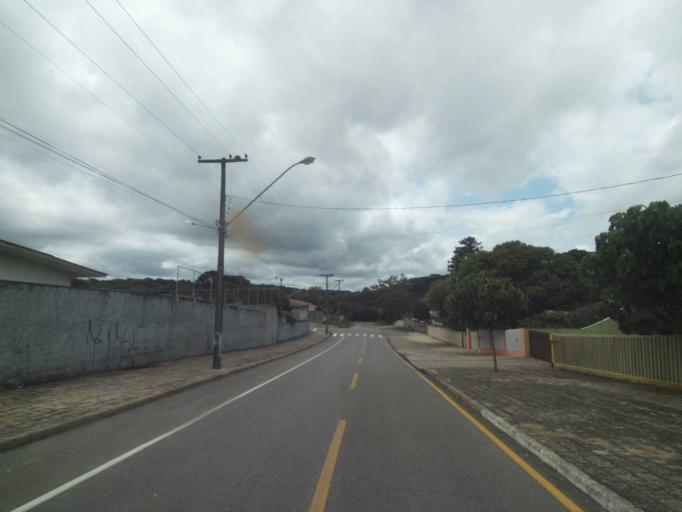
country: BR
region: Parana
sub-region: Campina Grande Do Sul
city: Campina Grande do Sul
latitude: -25.3061
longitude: -49.0523
